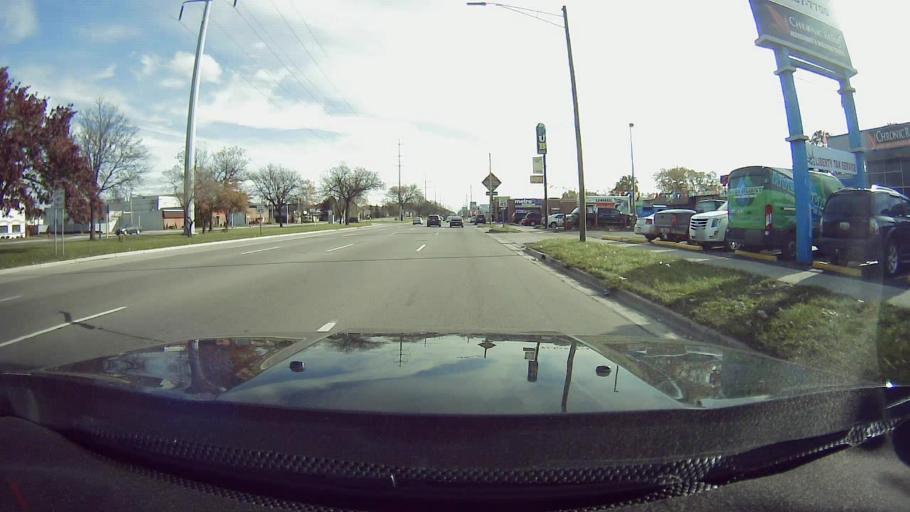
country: US
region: Michigan
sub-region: Oakland County
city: Southfield
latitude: 42.4432
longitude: -83.2577
